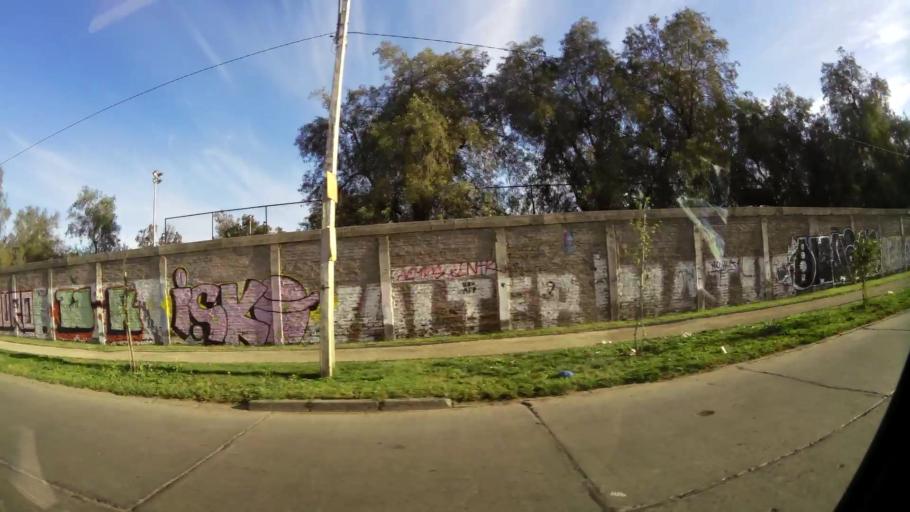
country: CL
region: Santiago Metropolitan
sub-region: Provincia de Santiago
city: Lo Prado
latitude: -33.4376
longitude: -70.7147
